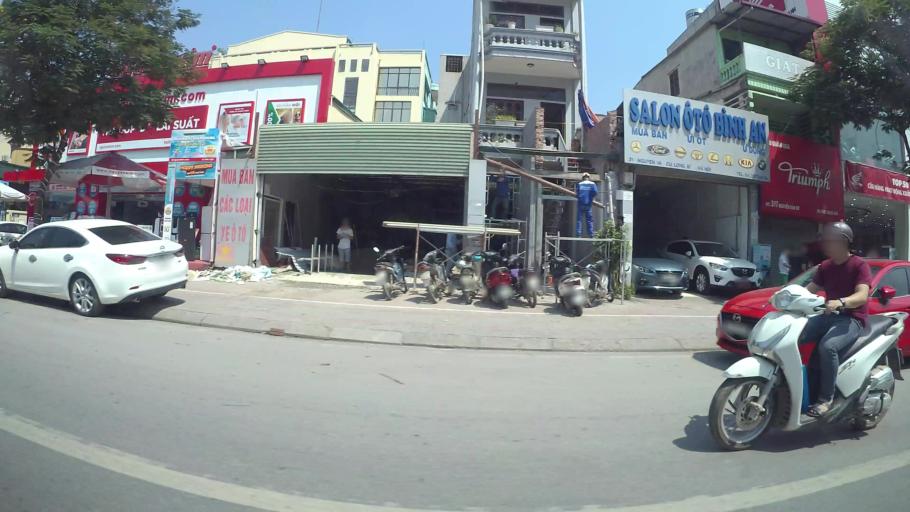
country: VN
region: Ha Noi
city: Hoan Kiem
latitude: 21.0457
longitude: 105.8756
